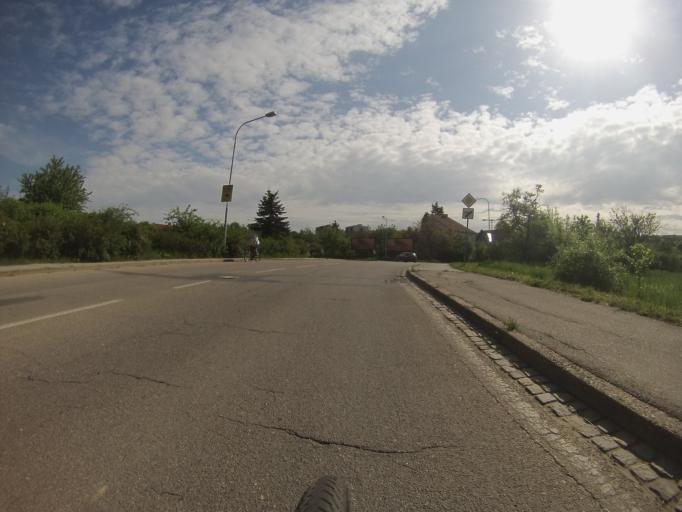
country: CZ
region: South Moravian
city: Troubsko
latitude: 49.2254
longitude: 16.5182
